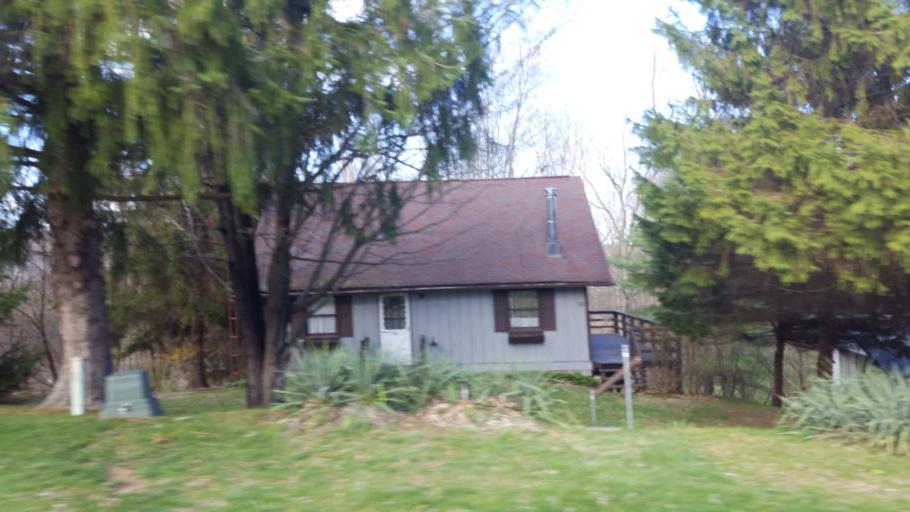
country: US
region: Ohio
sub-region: Knox County
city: Gambier
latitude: 40.4373
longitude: -82.3504
